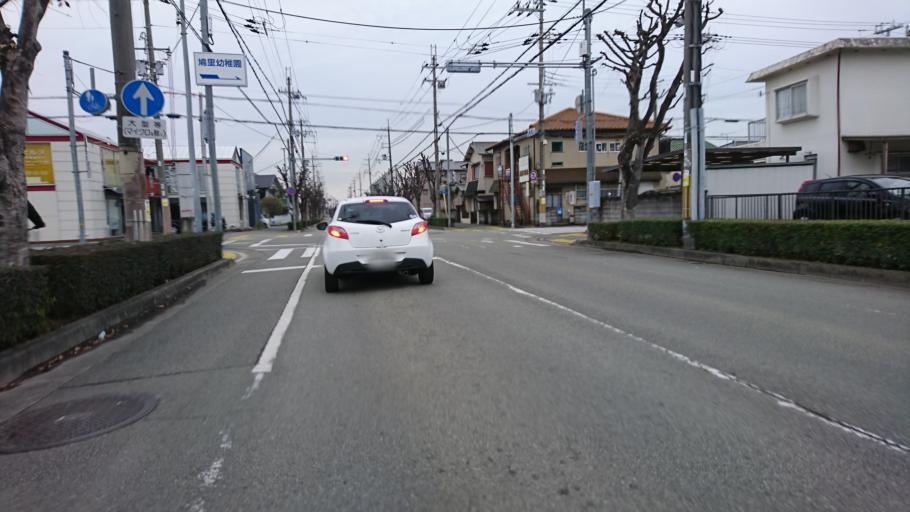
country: JP
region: Hyogo
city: Kakogawacho-honmachi
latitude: 34.7629
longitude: 134.8242
